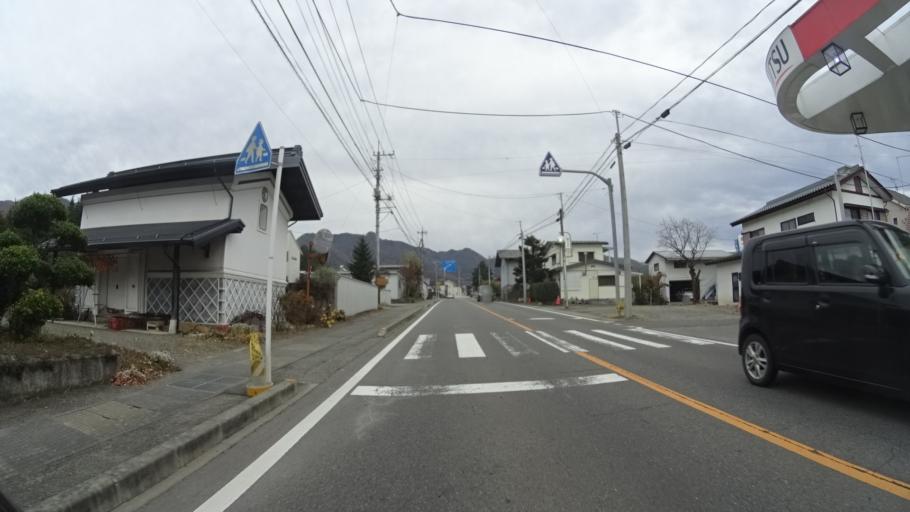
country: JP
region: Gunma
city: Numata
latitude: 36.6636
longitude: 139.1423
